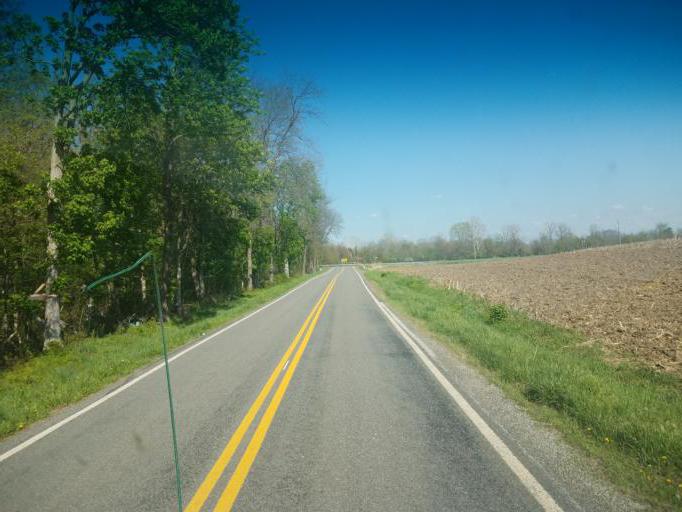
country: US
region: Ohio
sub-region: Medina County
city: Westfield Center
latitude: 41.0009
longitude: -81.9434
